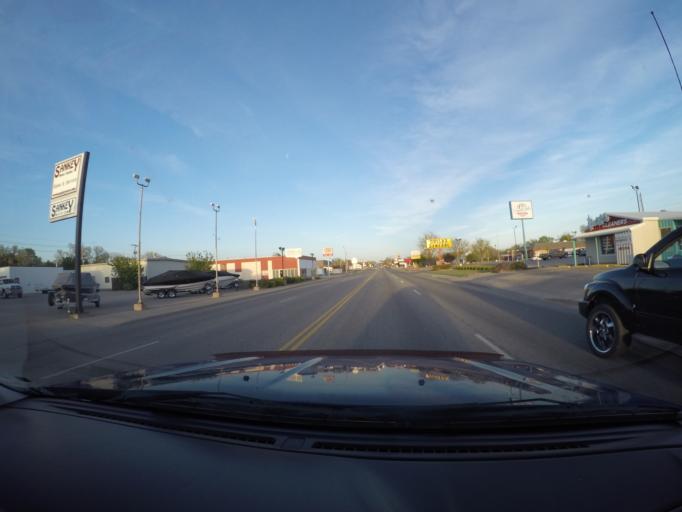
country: US
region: Kansas
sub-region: Saline County
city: Salina
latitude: 38.8271
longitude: -97.5979
